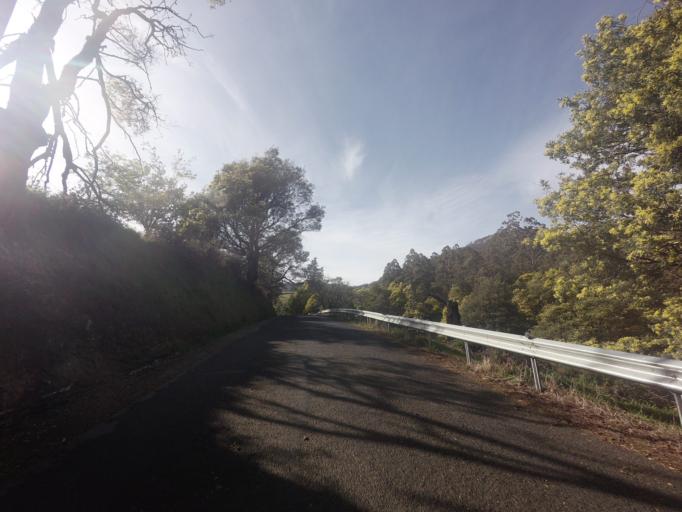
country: AU
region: Tasmania
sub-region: Kingborough
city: Kettering
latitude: -43.1731
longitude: 147.1661
